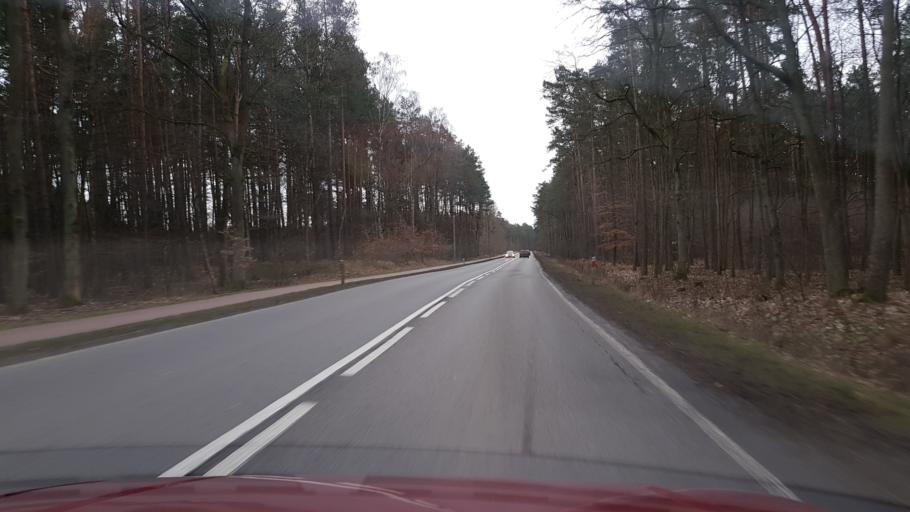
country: PL
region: West Pomeranian Voivodeship
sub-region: Powiat policki
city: Dobra
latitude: 53.5139
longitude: 14.4738
